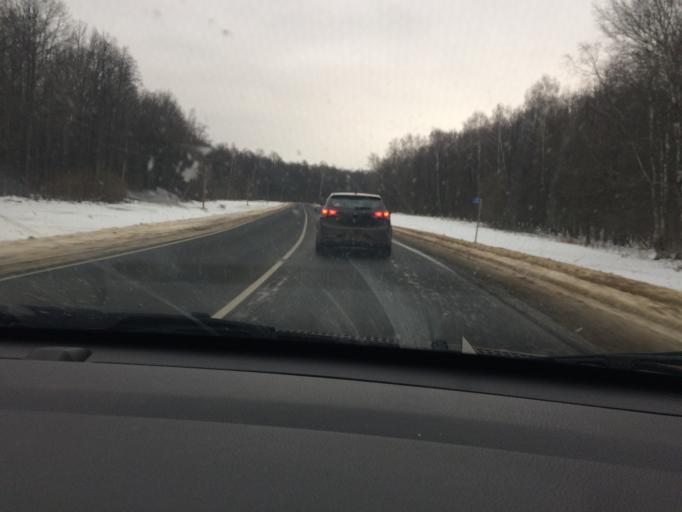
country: RU
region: Tula
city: Venev
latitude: 54.3356
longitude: 38.1080
